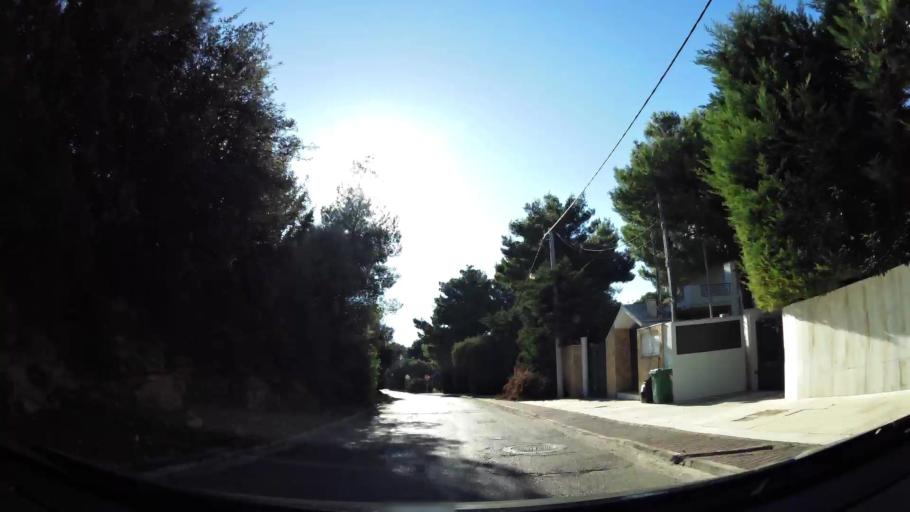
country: GR
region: Attica
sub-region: Nomarchia Athinas
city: Ekali
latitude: 38.1035
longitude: 23.8390
